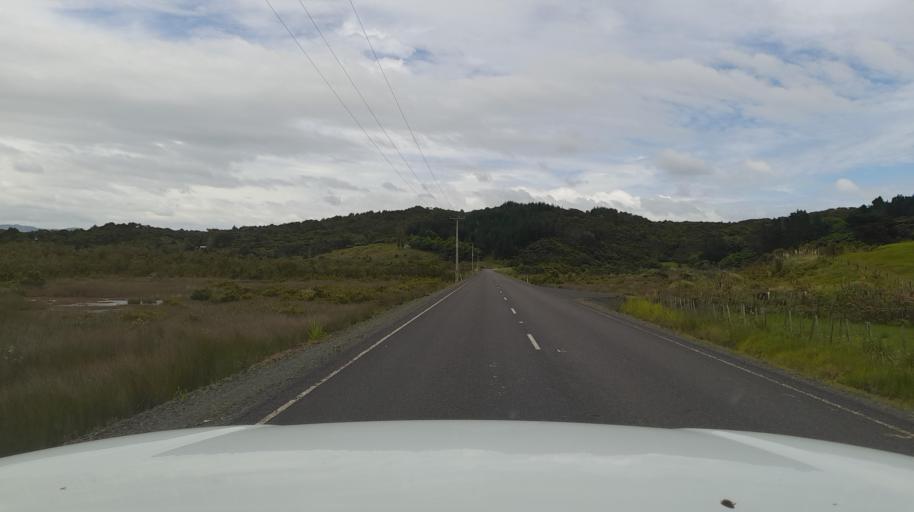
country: NZ
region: Northland
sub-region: Far North District
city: Kaitaia
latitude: -35.4037
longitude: 173.3821
